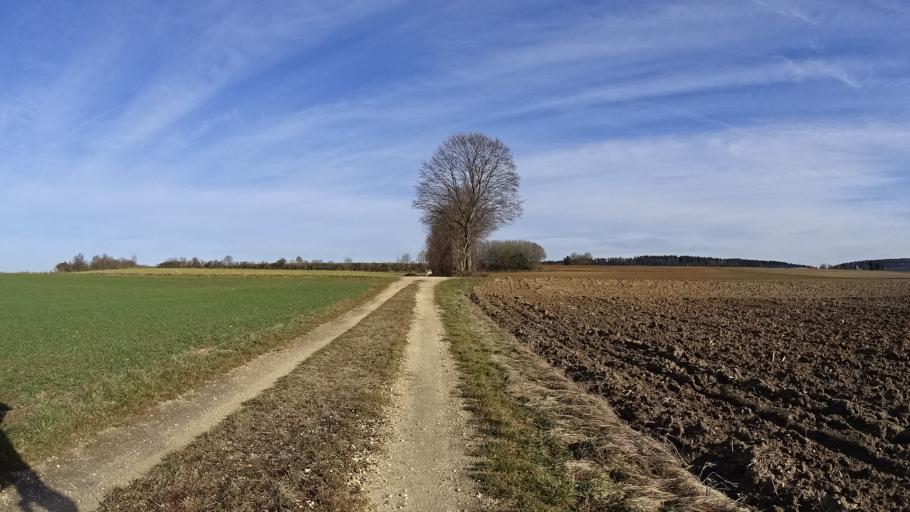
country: DE
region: Bavaria
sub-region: Upper Bavaria
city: Eitensheim
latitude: 48.8331
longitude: 11.3415
